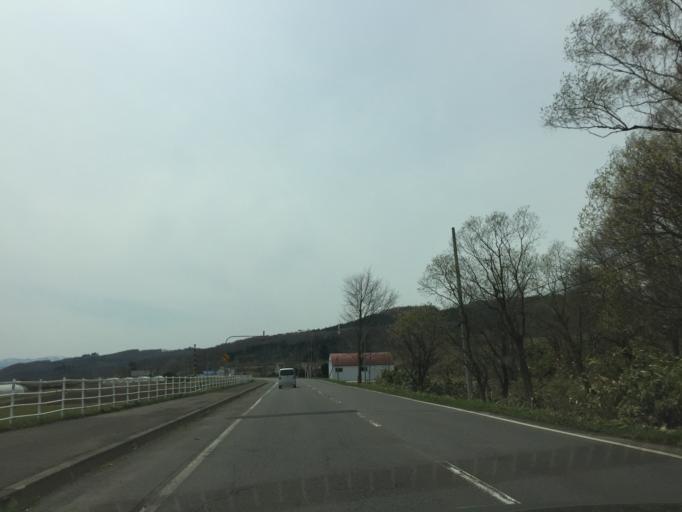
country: JP
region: Hokkaido
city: Ashibetsu
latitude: 43.5947
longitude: 142.2002
